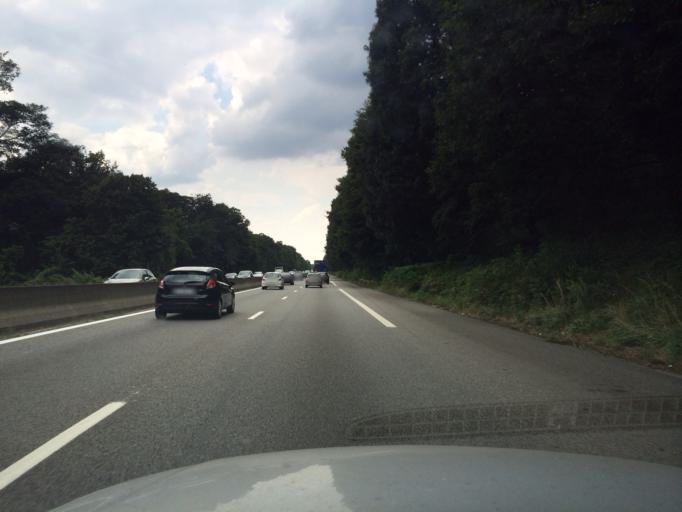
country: FR
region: Ile-de-France
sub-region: Departement des Yvelines
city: Noisy-le-Roi
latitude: 48.8562
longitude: 2.0567
